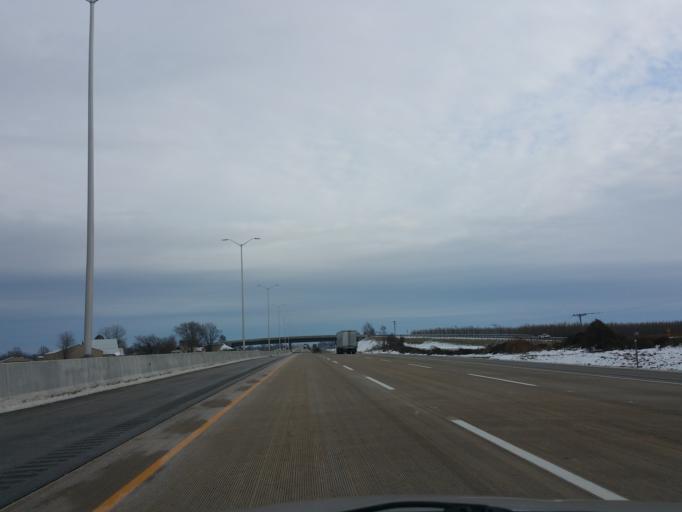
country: US
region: Illinois
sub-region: McHenry County
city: Marengo
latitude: 42.1961
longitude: -88.6712
